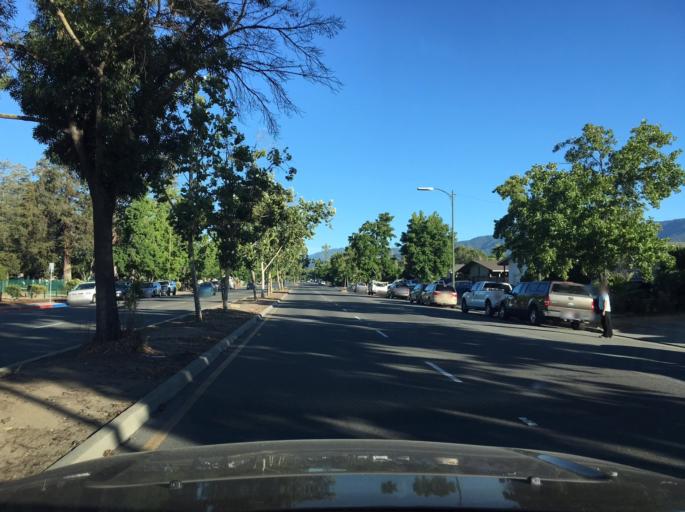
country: US
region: California
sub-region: Santa Clara County
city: Cambrian Park
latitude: 37.2602
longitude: -121.9181
